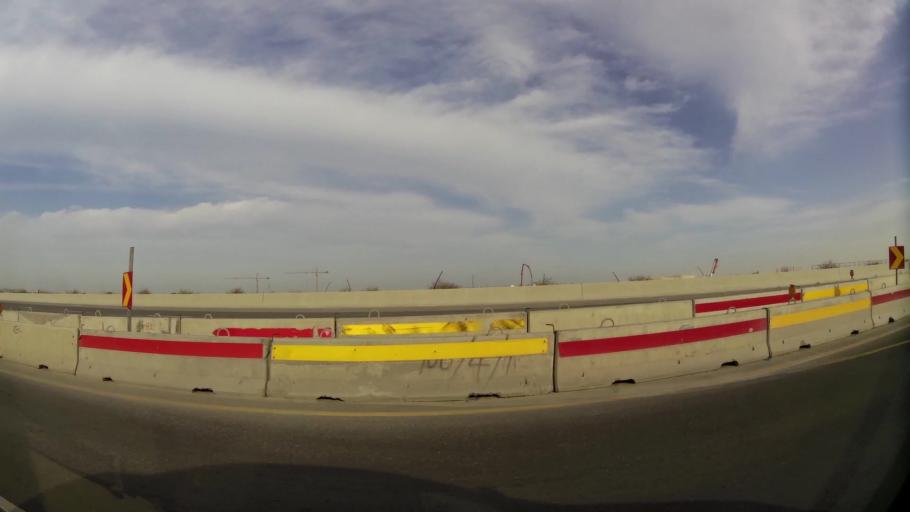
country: QA
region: Al Wakrah
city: Al Wakrah
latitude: 25.2284
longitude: 51.5921
